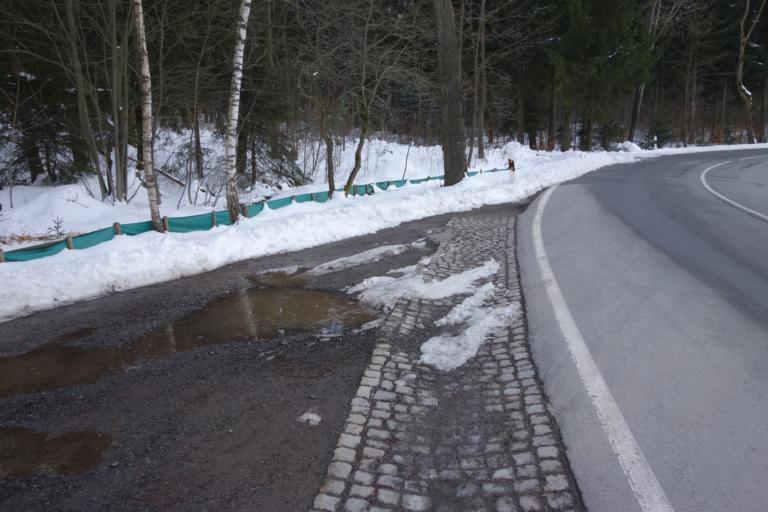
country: DE
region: Saxony
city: Eibenstock
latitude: 50.4765
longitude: 12.6172
